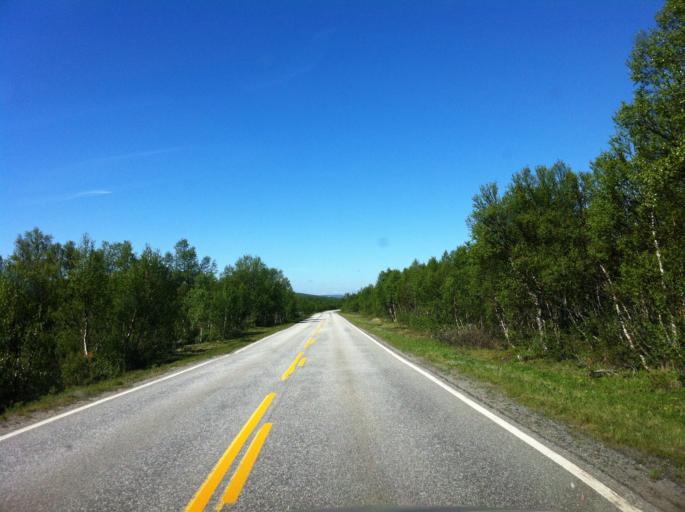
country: NO
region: Sor-Trondelag
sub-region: Tydal
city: Aas
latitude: 62.6392
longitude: 12.0057
